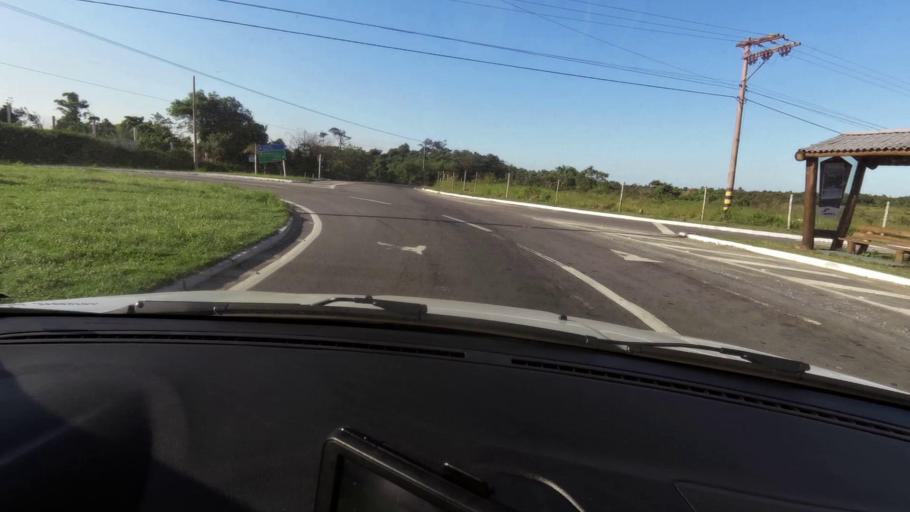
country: BR
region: Espirito Santo
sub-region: Piuma
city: Piuma
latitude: -20.7990
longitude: -40.5962
